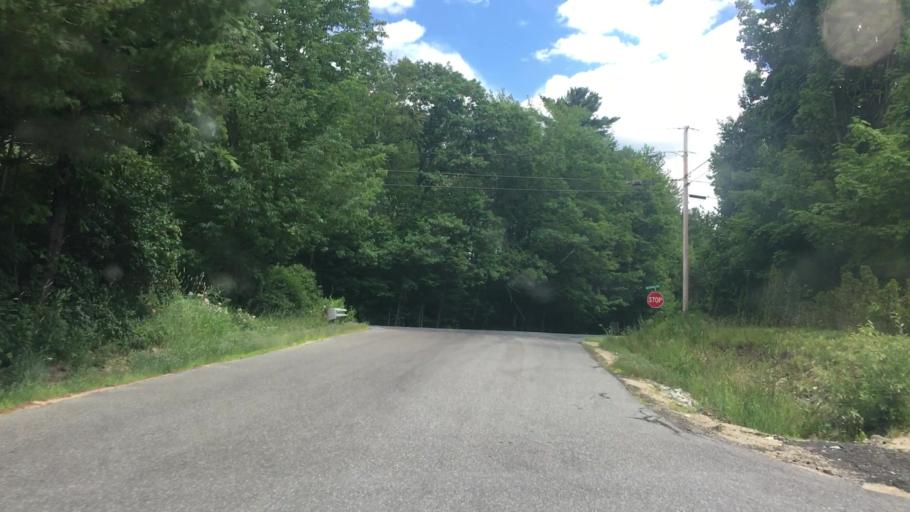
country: US
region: Maine
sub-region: Franklin County
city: Jay
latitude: 44.5376
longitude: -70.2165
